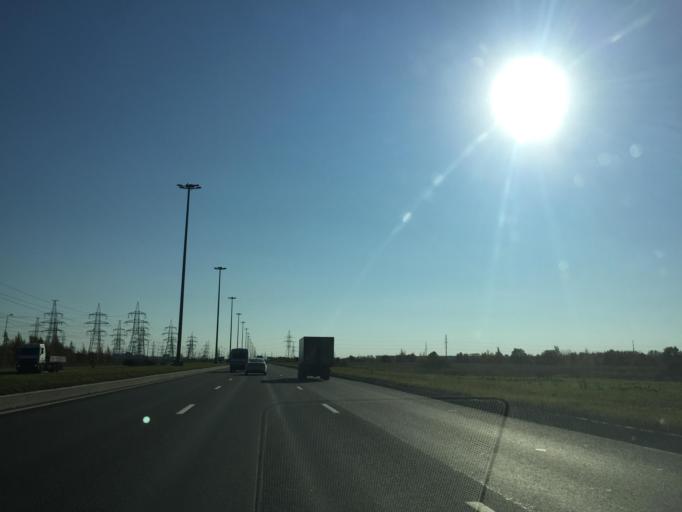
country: RU
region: St.-Petersburg
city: Petro-Slavyanka
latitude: 59.7577
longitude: 30.5161
